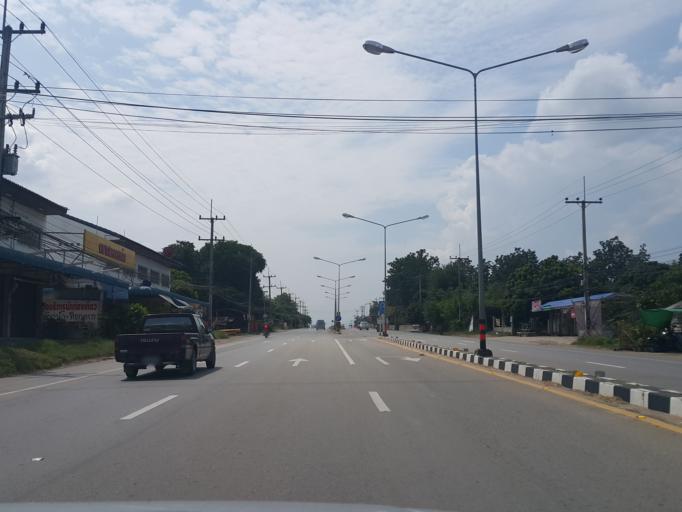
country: TH
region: Chiang Mai
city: Doi Lo
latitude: 18.4661
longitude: 98.7842
